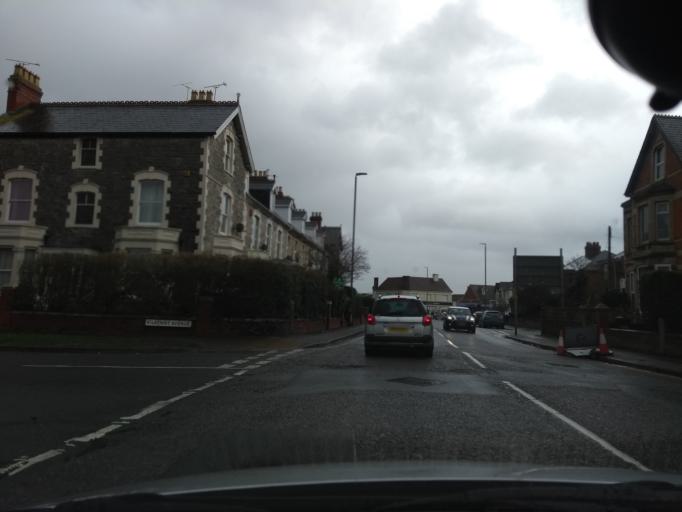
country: GB
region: England
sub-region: Somerset
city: Taunton
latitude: 51.0252
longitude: -3.1014
